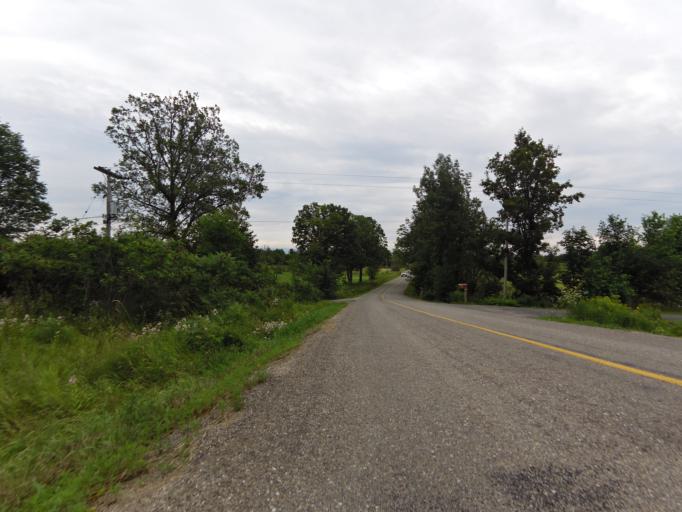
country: CA
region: Ontario
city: Kingston
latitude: 44.6281
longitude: -76.6494
